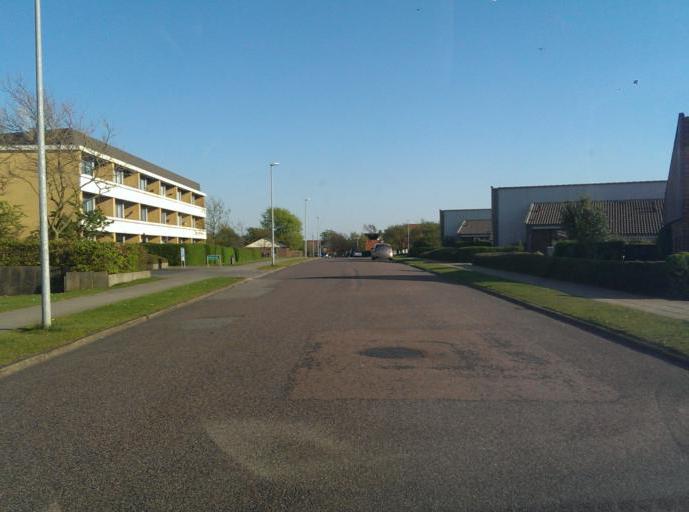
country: DK
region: South Denmark
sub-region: Esbjerg Kommune
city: Esbjerg
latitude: 55.4693
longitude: 8.4839
